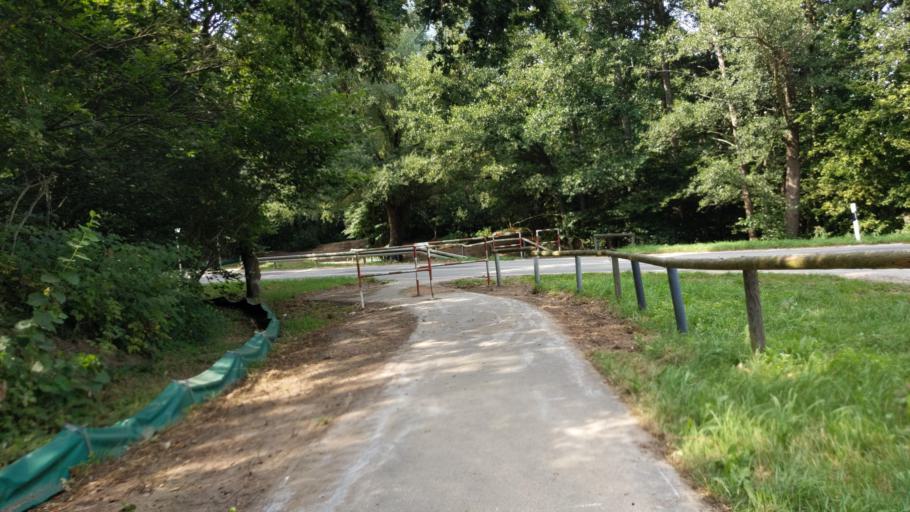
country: DE
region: Mecklenburg-Vorpommern
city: Selmsdorf
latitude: 53.8283
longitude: 10.8541
